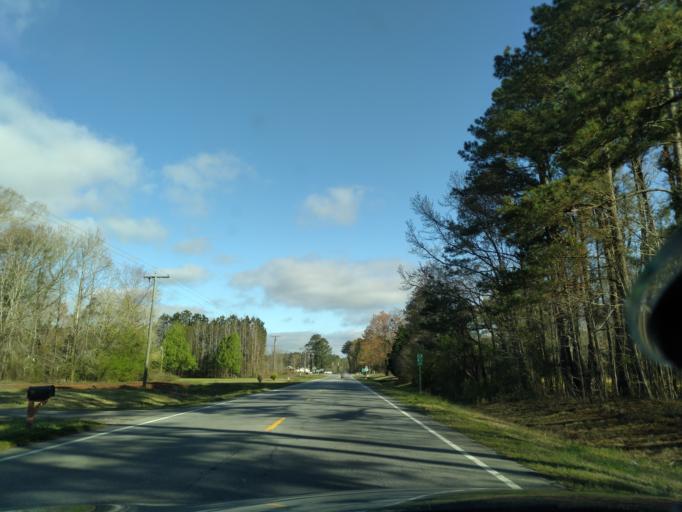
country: US
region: North Carolina
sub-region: Bertie County
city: Windsor
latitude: 36.0316
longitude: -76.7836
